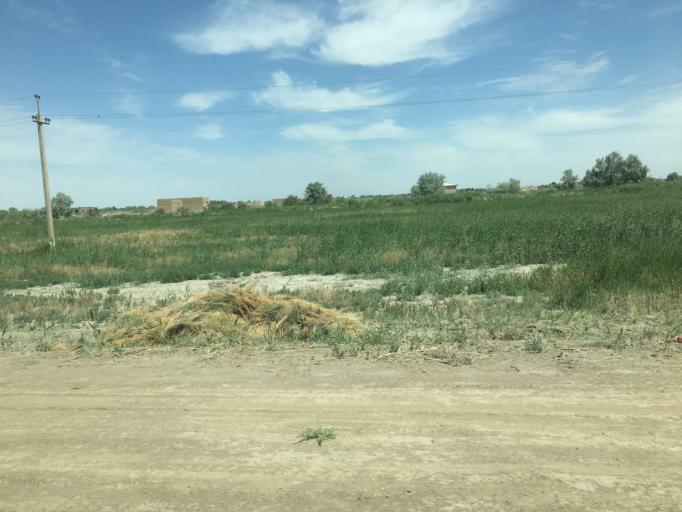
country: TM
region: Dasoguz
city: Tagta
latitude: 41.7076
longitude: 59.9369
